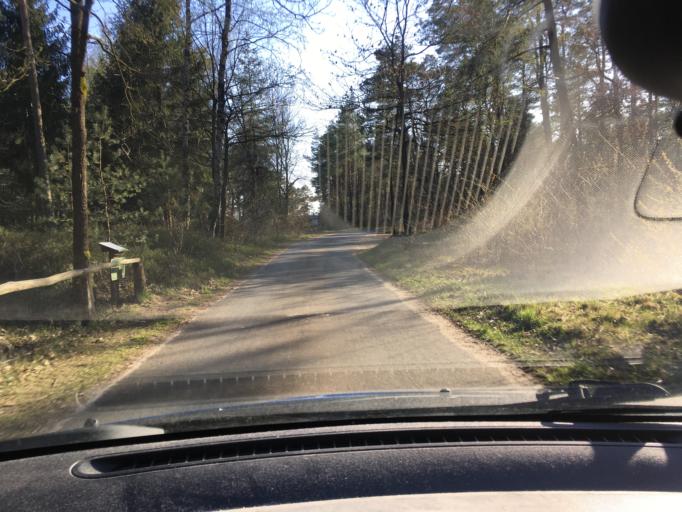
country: DE
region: Lower Saxony
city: Bispingen
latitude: 53.1073
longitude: 10.0101
